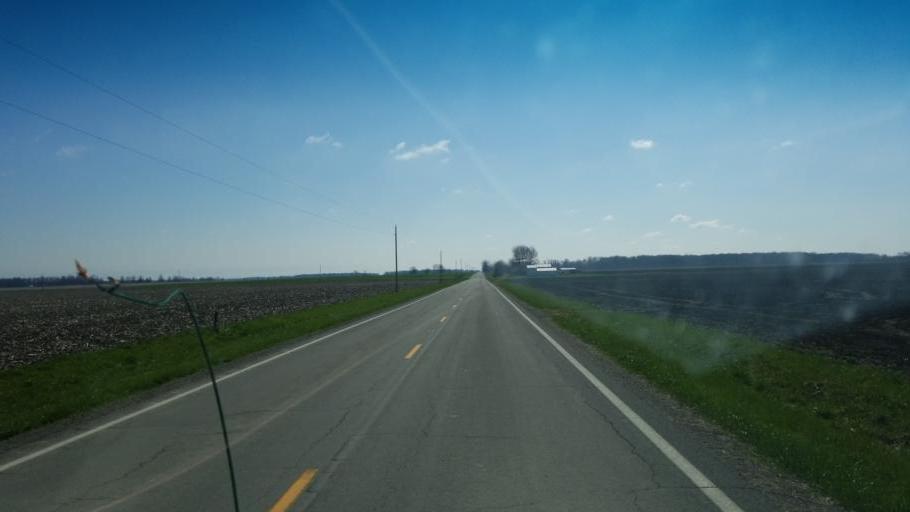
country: US
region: Ohio
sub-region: Wyandot County
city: Upper Sandusky
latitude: 40.7379
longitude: -83.3093
